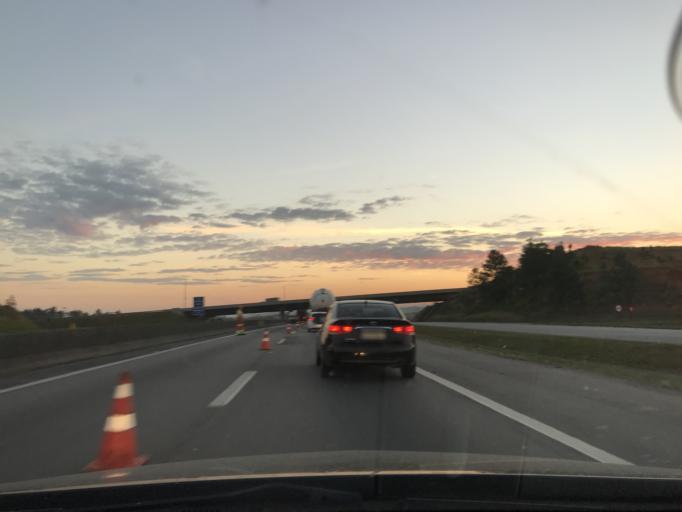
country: BR
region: Sao Paulo
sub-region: Jacarei
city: Jacarei
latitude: -23.3073
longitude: -46.0423
